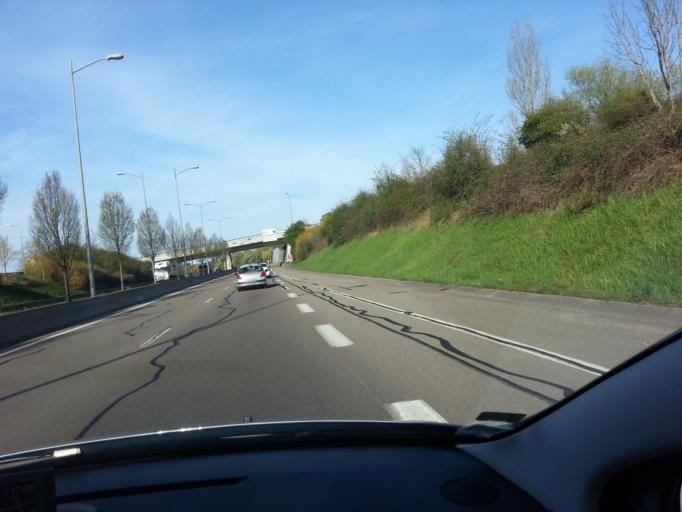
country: FR
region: Franche-Comte
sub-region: Departement du Doubs
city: Besancon
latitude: 47.2574
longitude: 5.9990
